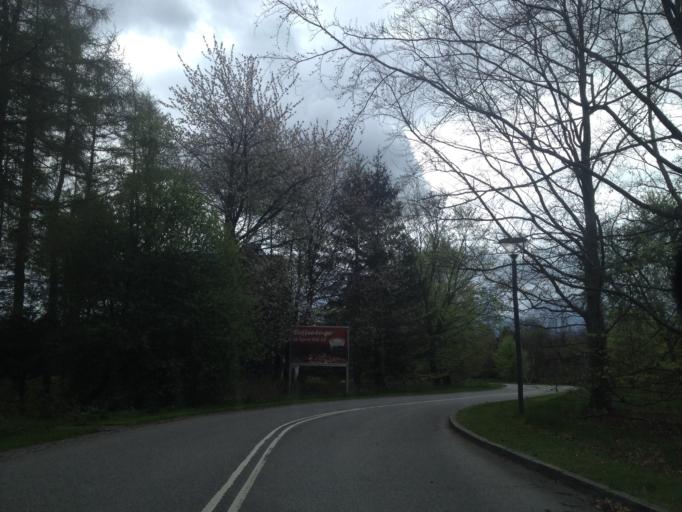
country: DK
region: Capital Region
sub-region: Horsholm Kommune
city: Horsholm
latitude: 55.8702
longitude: 12.4900
